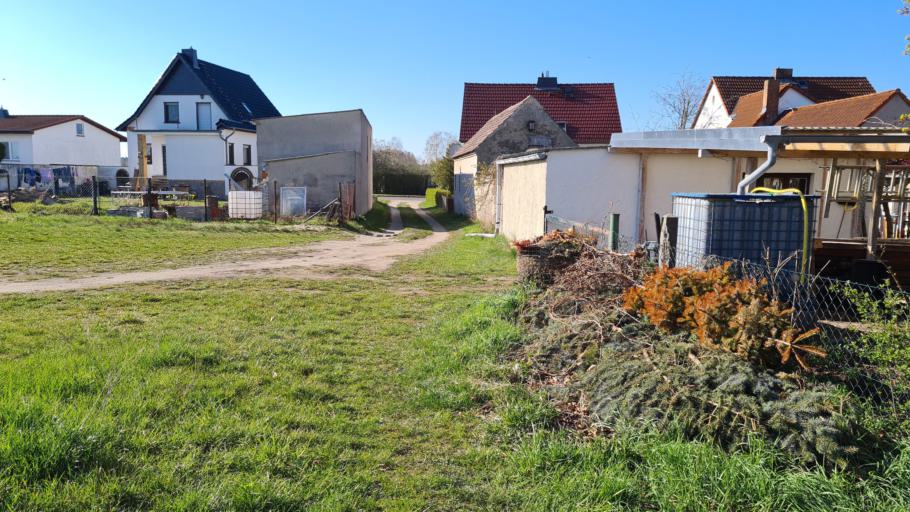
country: DE
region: Brandenburg
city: Ruckersdorf
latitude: 51.5538
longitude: 13.5979
